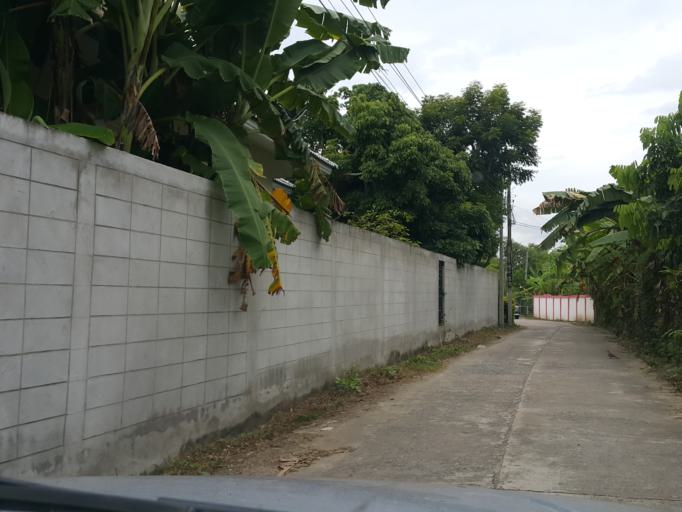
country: TH
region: Chiang Mai
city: San Sai
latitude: 18.8397
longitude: 99.1245
